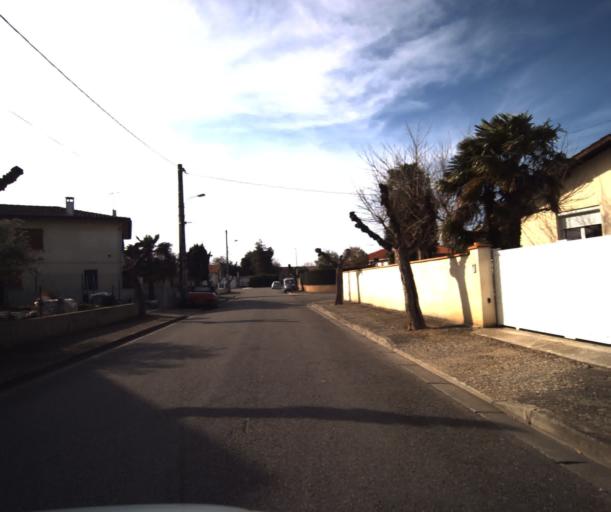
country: FR
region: Midi-Pyrenees
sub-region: Departement du Tarn-et-Garonne
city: Labastide-Saint-Pierre
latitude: 43.9168
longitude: 1.3712
